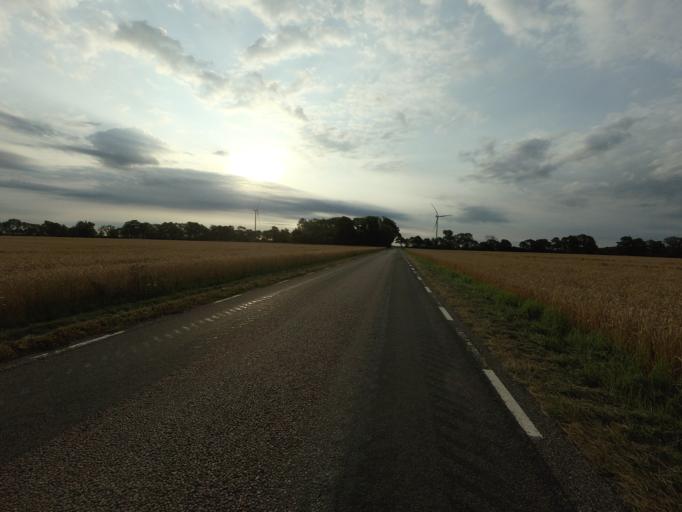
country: SE
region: Skane
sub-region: Helsingborg
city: Odakra
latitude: 56.1504
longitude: 12.6508
